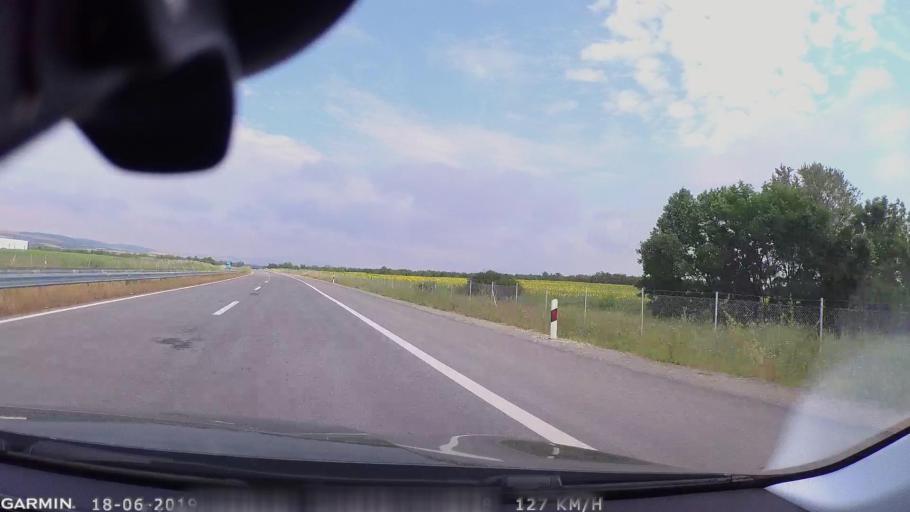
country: MK
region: Sveti Nikole
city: Sveti Nikole
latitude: 41.8275
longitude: 22.0048
